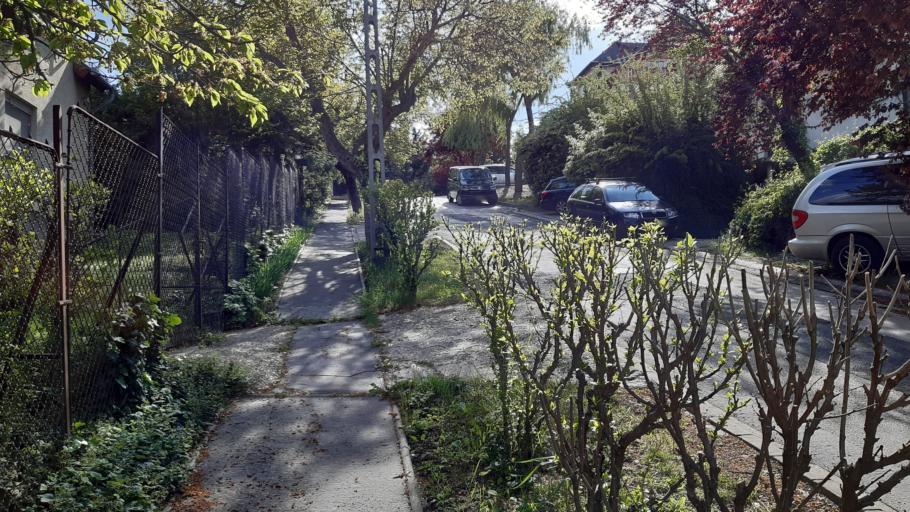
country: HU
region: Budapest
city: Budapest XXII. keruelet
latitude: 47.4451
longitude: 19.0239
